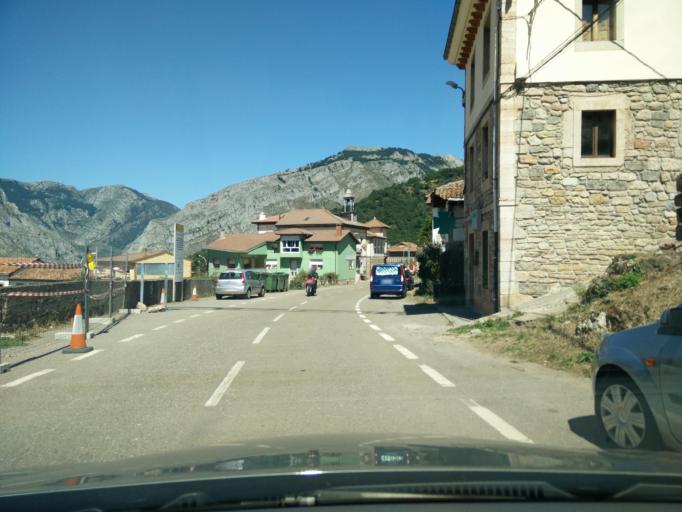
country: ES
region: Castille and Leon
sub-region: Provincia de Leon
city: Oseja de Sajambre
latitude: 43.1363
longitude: -5.0379
